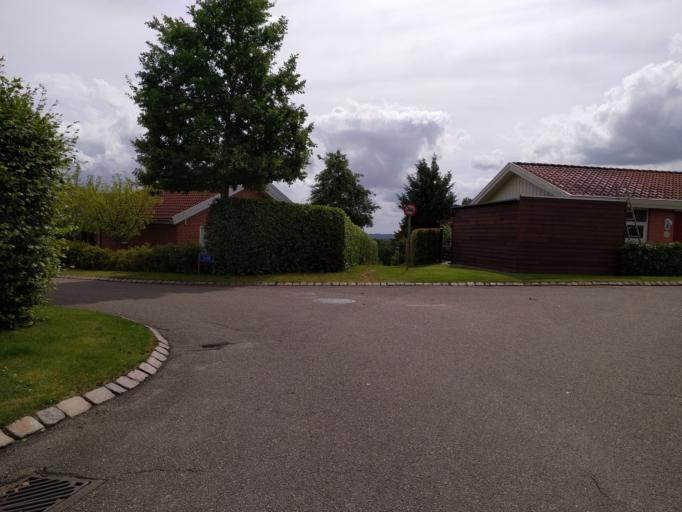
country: DK
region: Central Jutland
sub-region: Skanderborg Kommune
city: Ry
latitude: 56.0831
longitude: 9.7785
